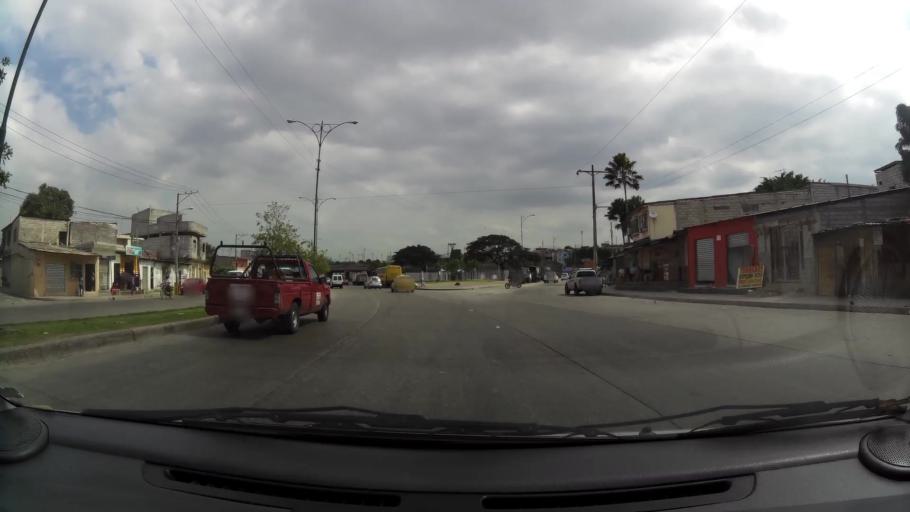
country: EC
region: Guayas
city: Santa Lucia
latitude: -2.0898
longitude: -79.9354
